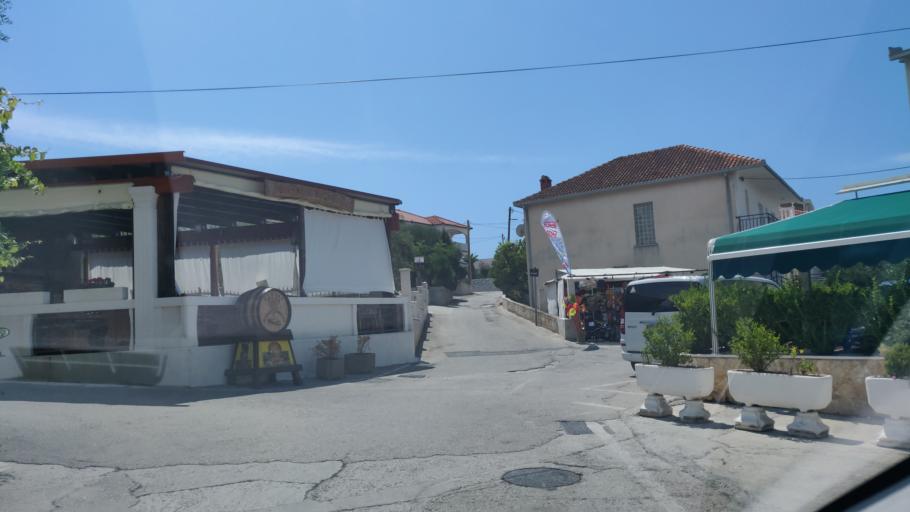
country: HR
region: Splitsko-Dalmatinska
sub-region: Grad Trogir
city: Trogir
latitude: 43.4955
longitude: 16.2607
